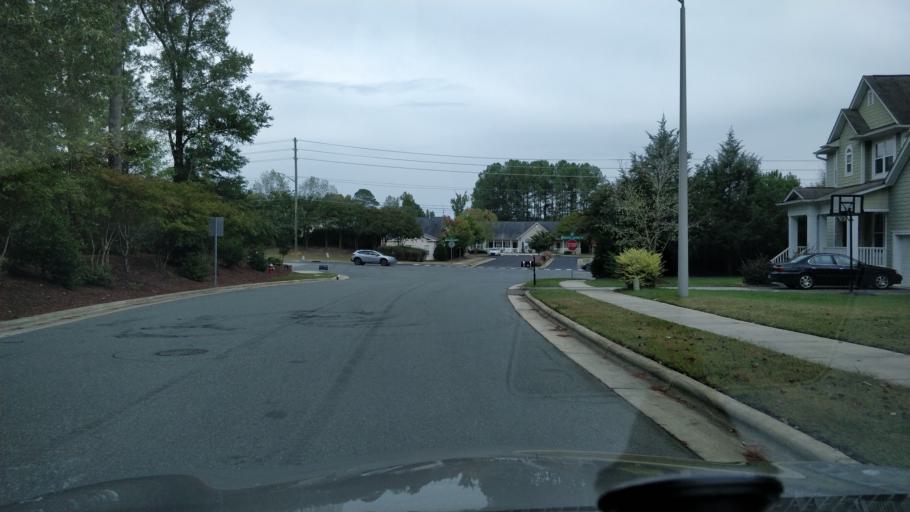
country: US
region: North Carolina
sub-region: Wake County
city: Morrisville
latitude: 35.8194
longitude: -78.8429
